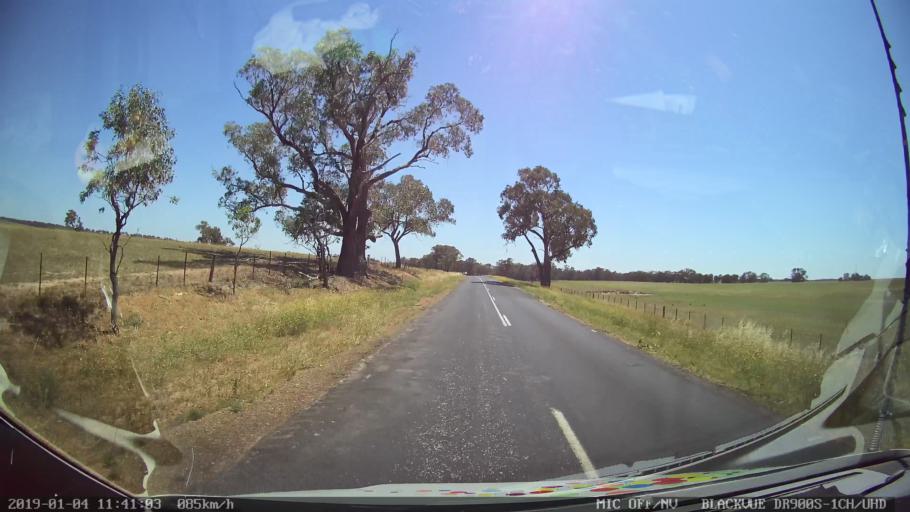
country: AU
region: New South Wales
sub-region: Cabonne
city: Molong
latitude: -32.9983
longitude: 148.7865
